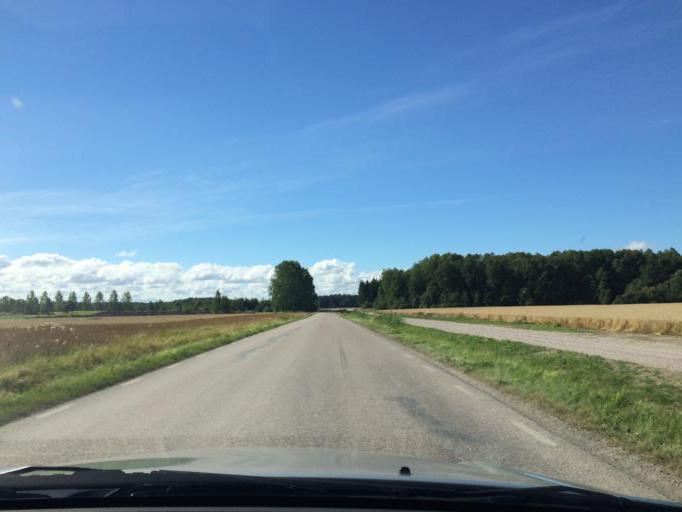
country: SE
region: Vaestmanland
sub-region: Vasteras
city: Vasteras
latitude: 59.5746
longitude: 16.4891
